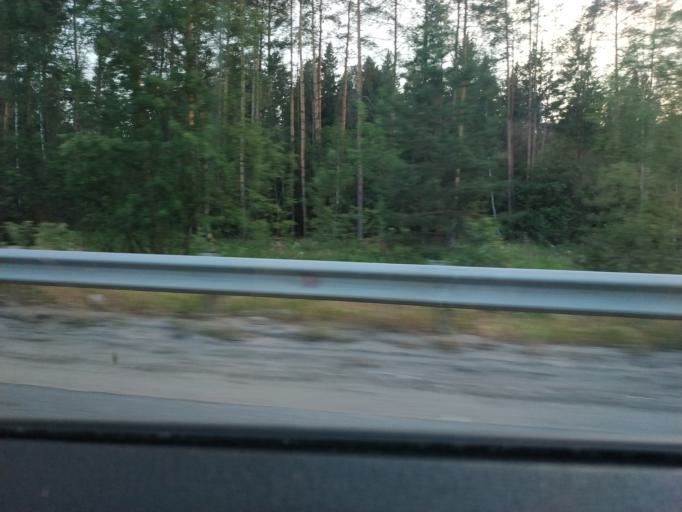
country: RU
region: Moskovskaya
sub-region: Shchelkovskiy Rayon
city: Grebnevo
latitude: 56.0023
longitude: 38.1295
